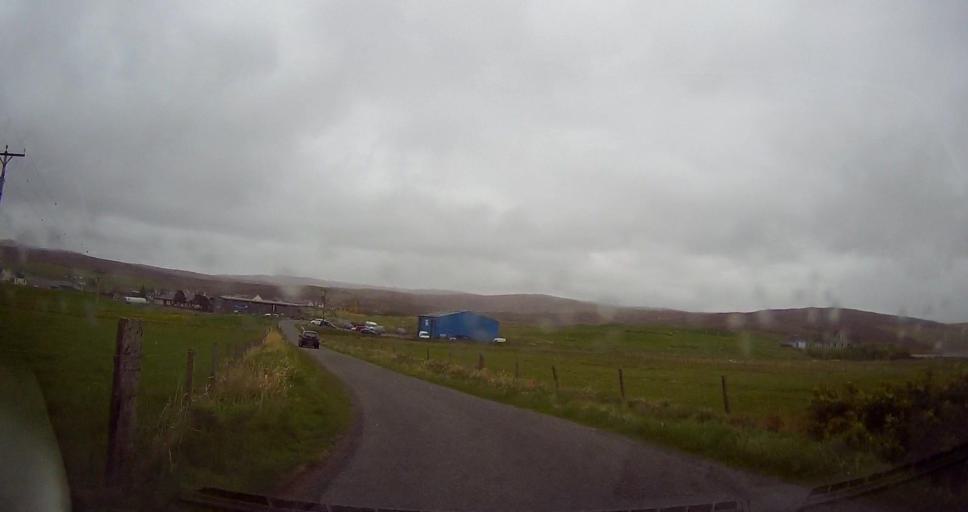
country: GB
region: Scotland
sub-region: Shetland Islands
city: Lerwick
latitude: 60.2842
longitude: -1.3835
